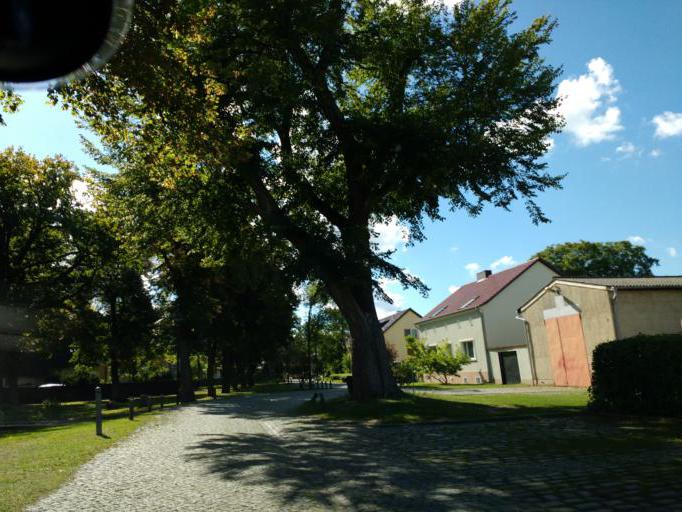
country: DE
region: Brandenburg
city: Mittenwalde
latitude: 52.2045
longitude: 13.5825
